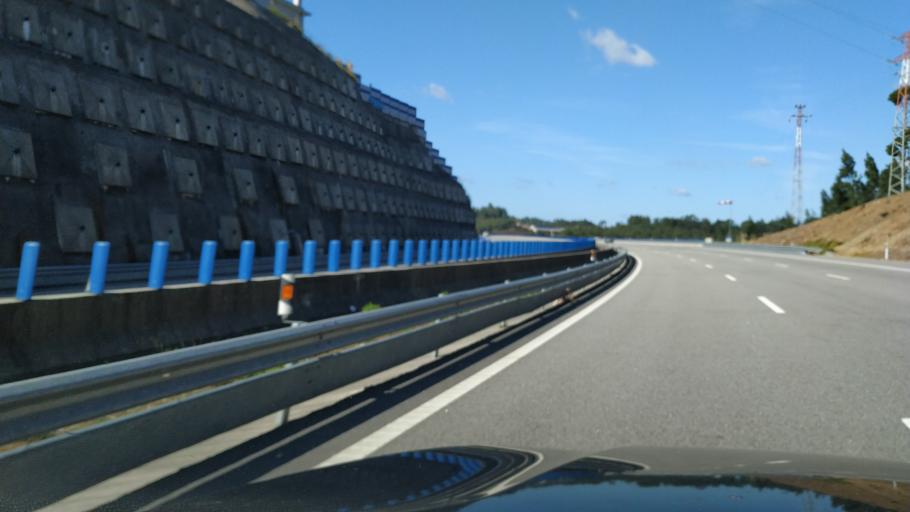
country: PT
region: Porto
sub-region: Vila Nova de Gaia
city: Olival
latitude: 41.0780
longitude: -8.5405
